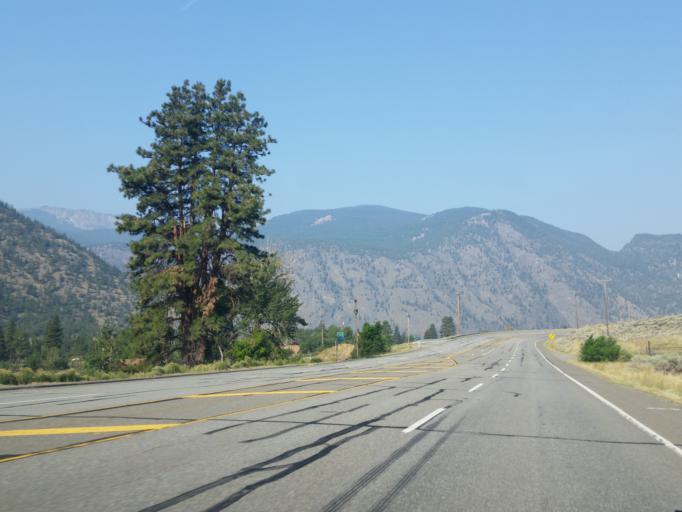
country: CA
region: British Columbia
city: Oliver
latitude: 49.2205
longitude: -119.9511
